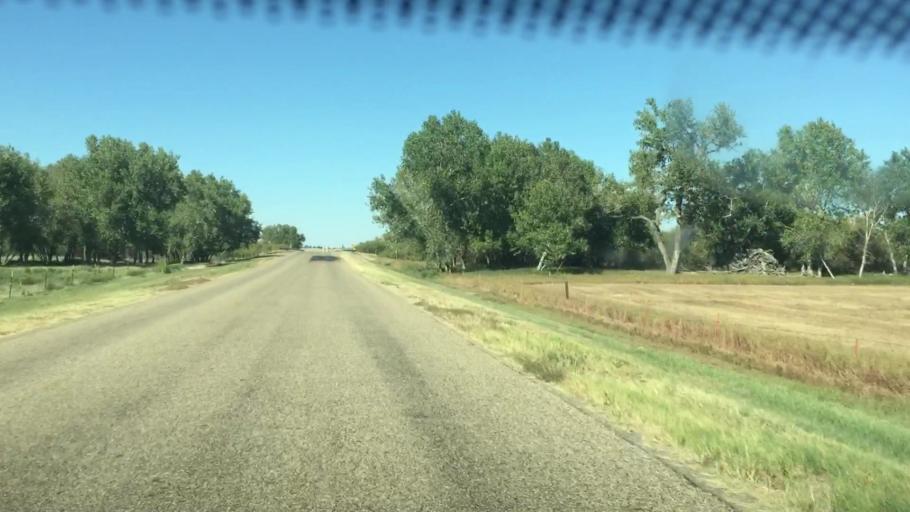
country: US
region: Colorado
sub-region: Prowers County
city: Lamar
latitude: 38.0944
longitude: -102.5196
